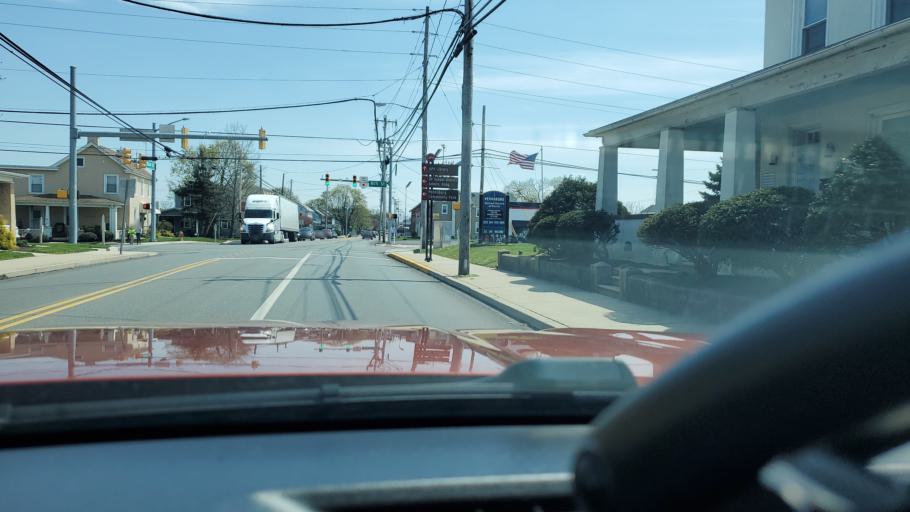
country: US
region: Pennsylvania
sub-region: Montgomery County
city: Pennsburg
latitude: 40.3913
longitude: -75.4923
